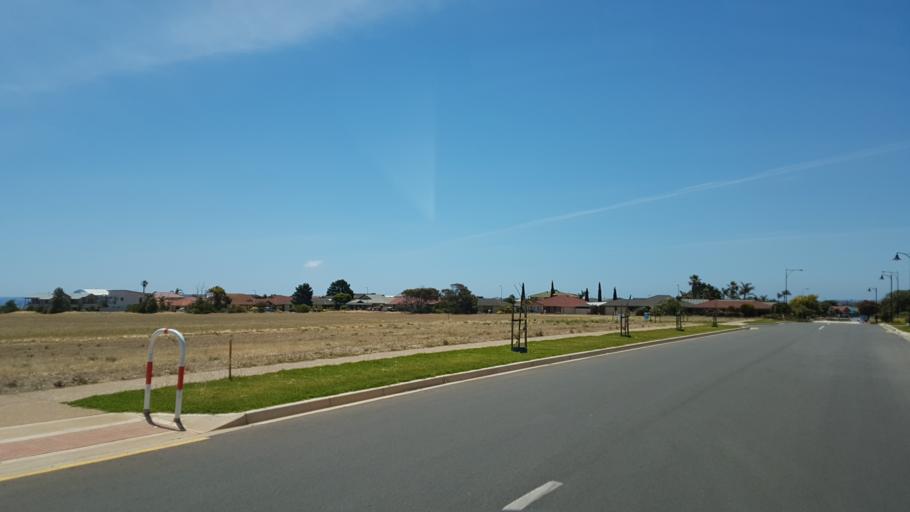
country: AU
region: South Australia
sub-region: Onkaparinga
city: Moana
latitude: -35.2177
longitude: 138.4752
